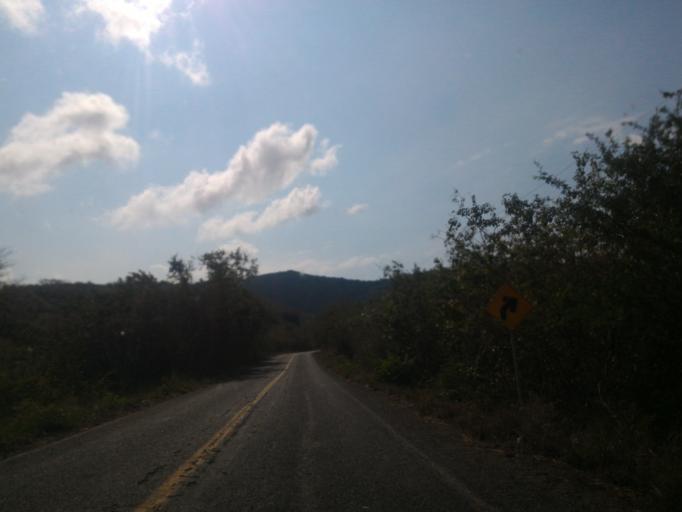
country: MX
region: Michoacan
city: Coahuayana Viejo
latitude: 18.5012
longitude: -103.5720
